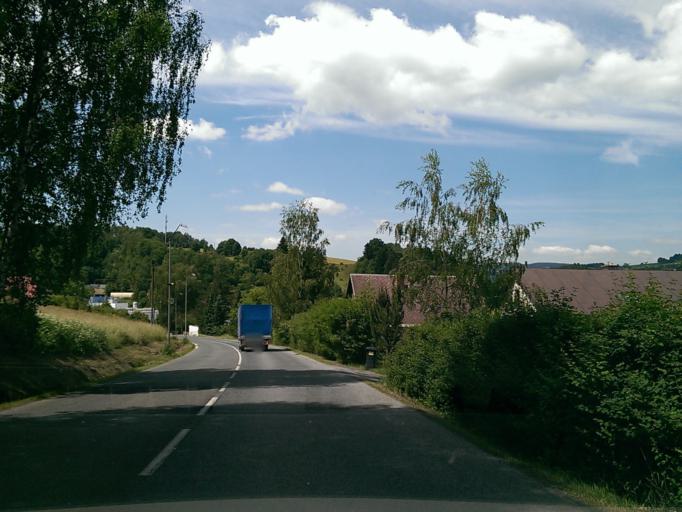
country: CZ
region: Liberecky
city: Zelezny Brod
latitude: 50.6371
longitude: 15.2665
